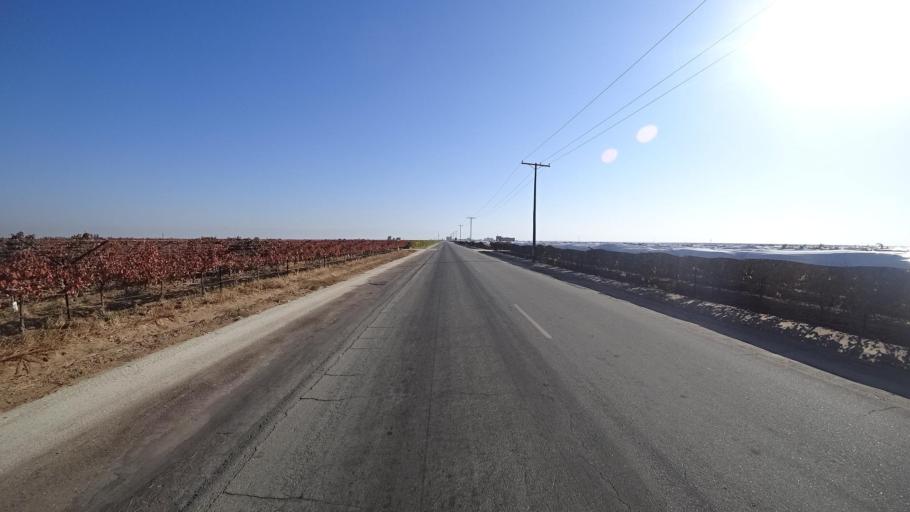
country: US
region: California
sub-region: Kern County
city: Delano
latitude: 35.7469
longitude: -119.2016
